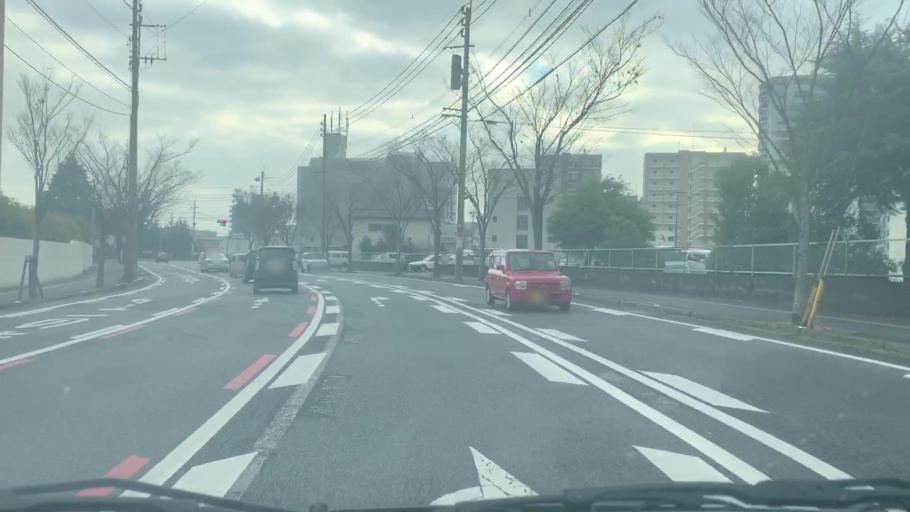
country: JP
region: Saga Prefecture
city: Saga-shi
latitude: 33.2640
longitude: 130.3022
